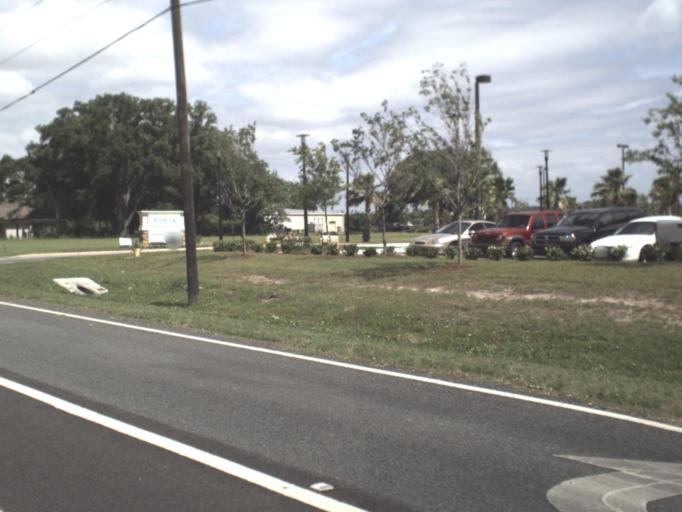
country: US
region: Florida
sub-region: Nassau County
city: Yulee
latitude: 30.6257
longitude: -81.5454
